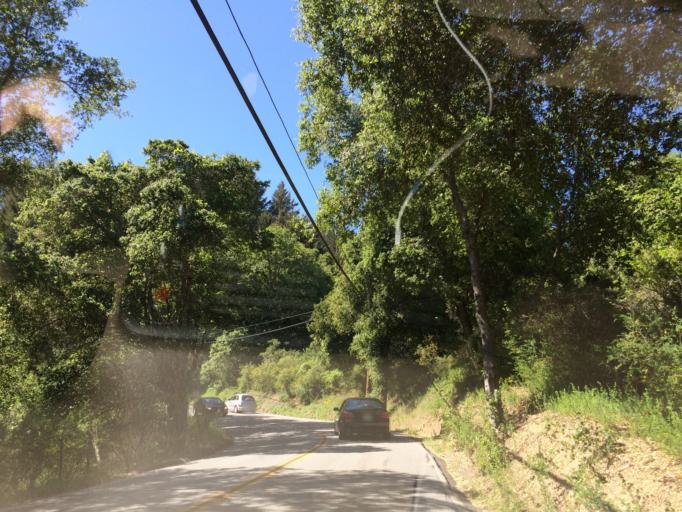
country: US
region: California
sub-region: Santa Clara County
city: Lexington Hills
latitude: 37.1725
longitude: -122.0126
